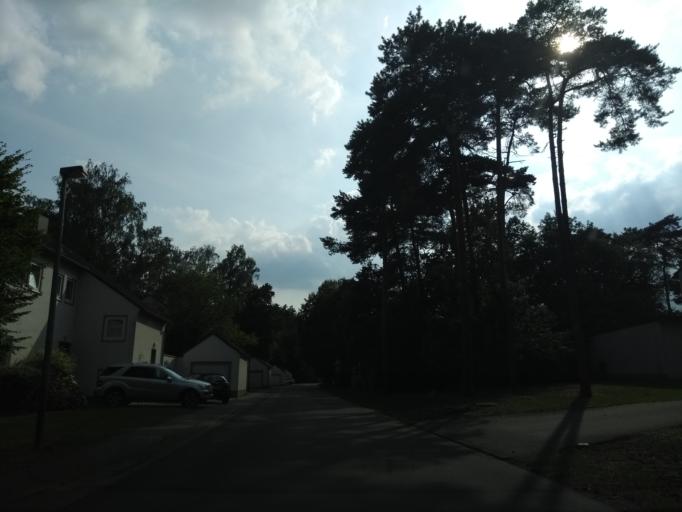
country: DE
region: North Rhine-Westphalia
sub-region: Regierungsbezirk Detmold
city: Paderborn
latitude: 51.7727
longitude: 8.7295
